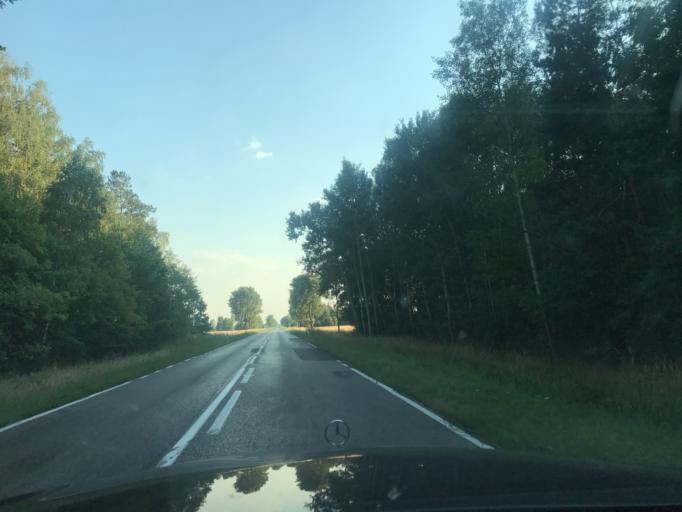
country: PL
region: Lublin Voivodeship
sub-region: Powiat parczewski
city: Jablon
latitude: 51.6918
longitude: 23.0363
